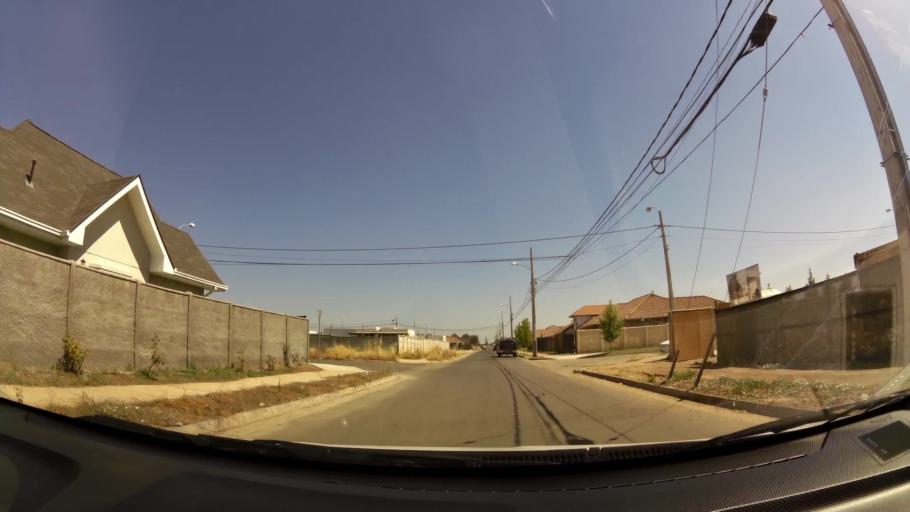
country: CL
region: Maule
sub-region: Provincia de Talca
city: Talca
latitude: -35.4383
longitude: -71.5953
